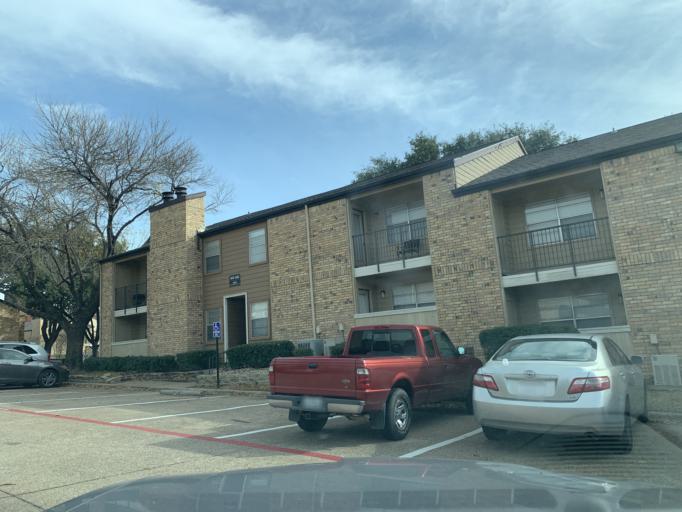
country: US
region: Texas
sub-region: Tarrant County
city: Euless
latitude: 32.7836
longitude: -97.0633
